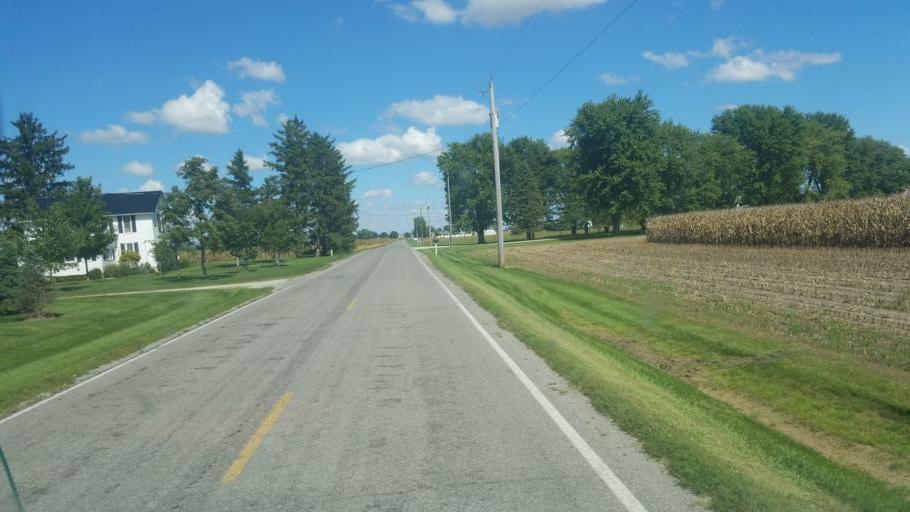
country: US
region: Ohio
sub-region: Madison County
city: Plain City
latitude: 40.0455
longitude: -83.3523
